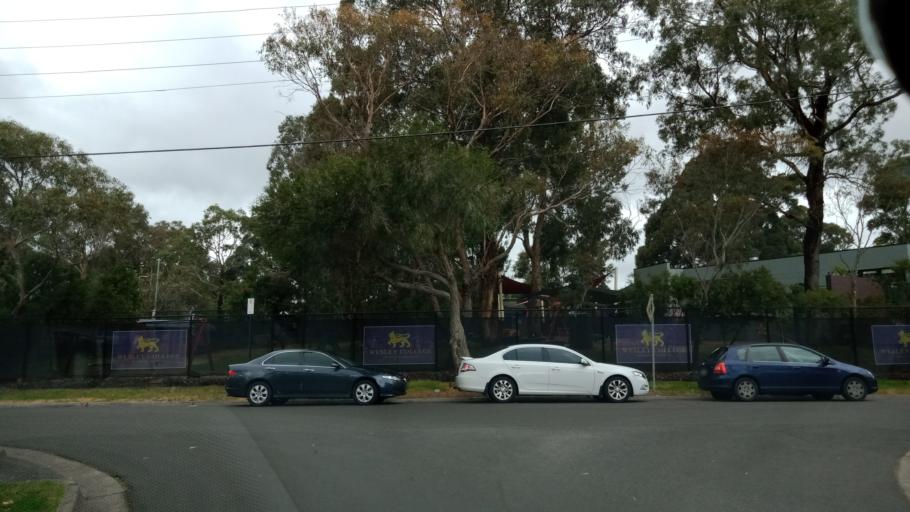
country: AU
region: Victoria
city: Burwood East
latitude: -37.8760
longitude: 145.1517
